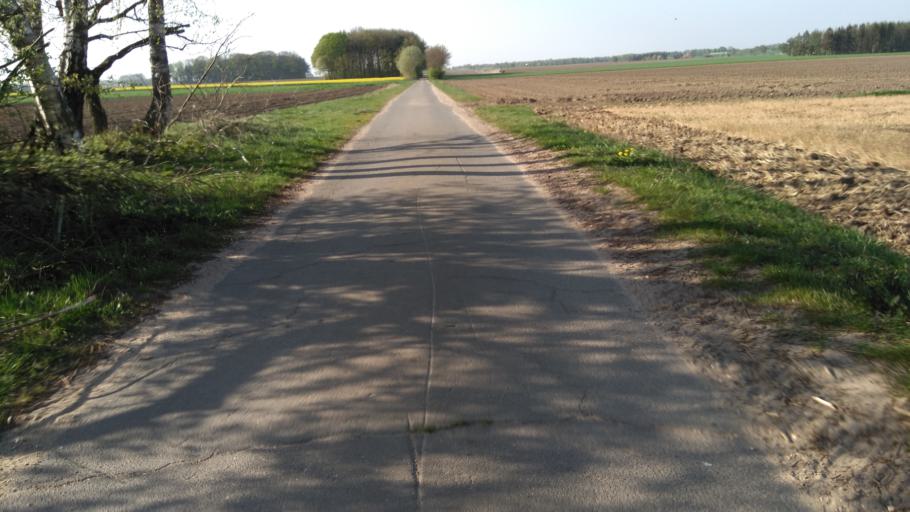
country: DE
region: Lower Saxony
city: Apensen
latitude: 53.4305
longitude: 9.6493
